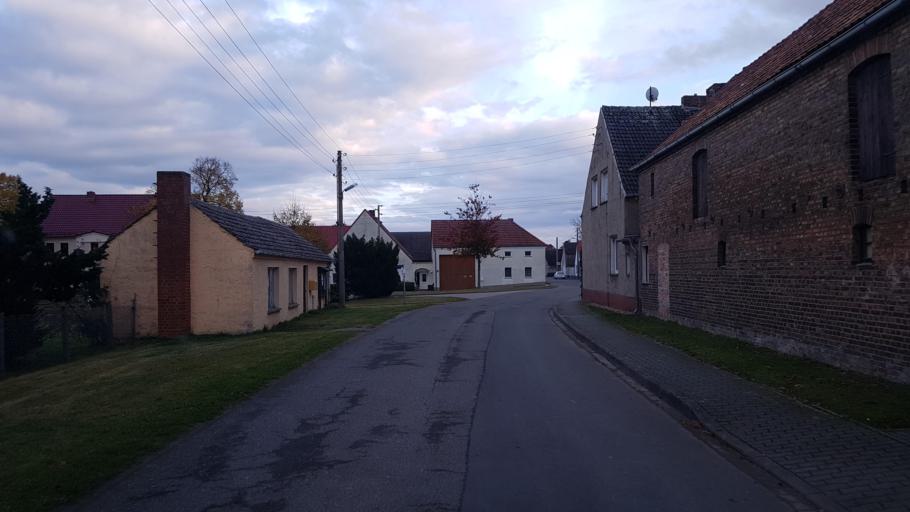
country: DE
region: Saxony-Anhalt
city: Seyda
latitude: 51.9245
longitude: 12.8883
